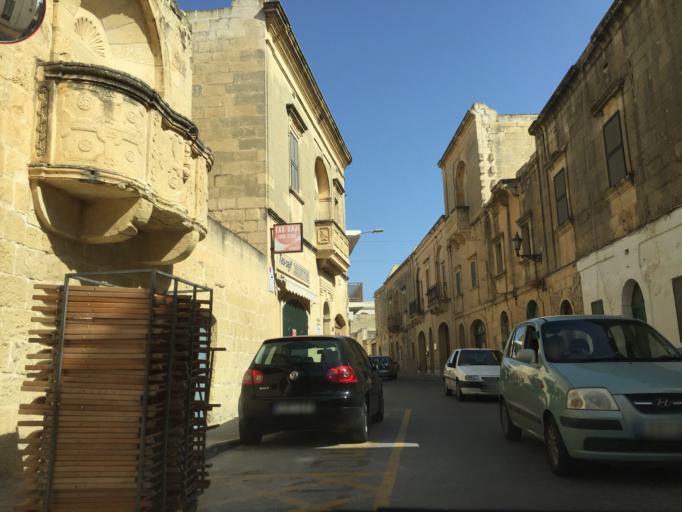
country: MT
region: L-Gharb
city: Gharb
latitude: 36.0594
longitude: 14.2094
